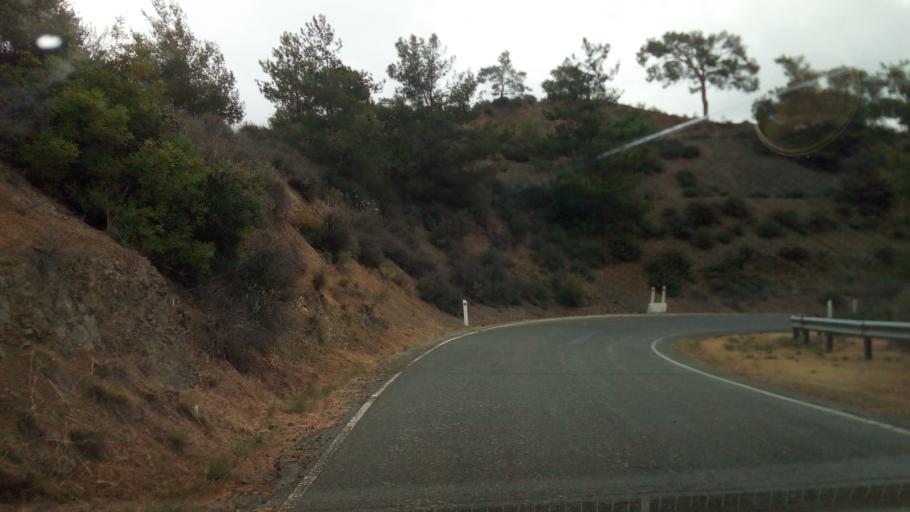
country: CY
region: Limassol
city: Parekklisha
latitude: 34.8645
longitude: 33.1838
